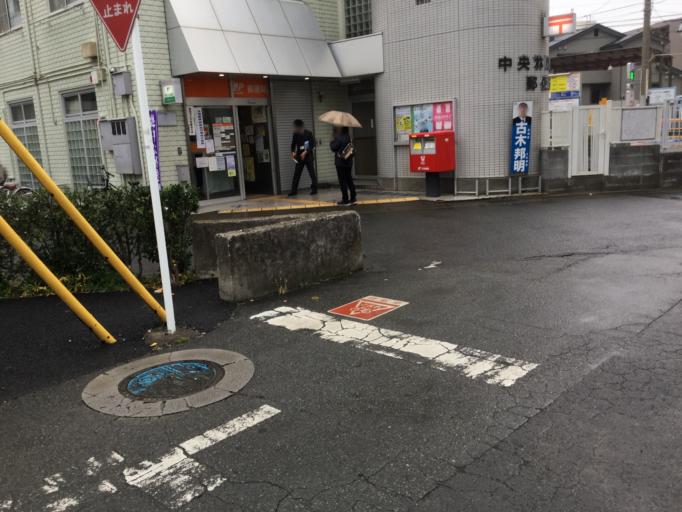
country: JP
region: Kanagawa
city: Minami-rinkan
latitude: 35.5074
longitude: 139.4432
